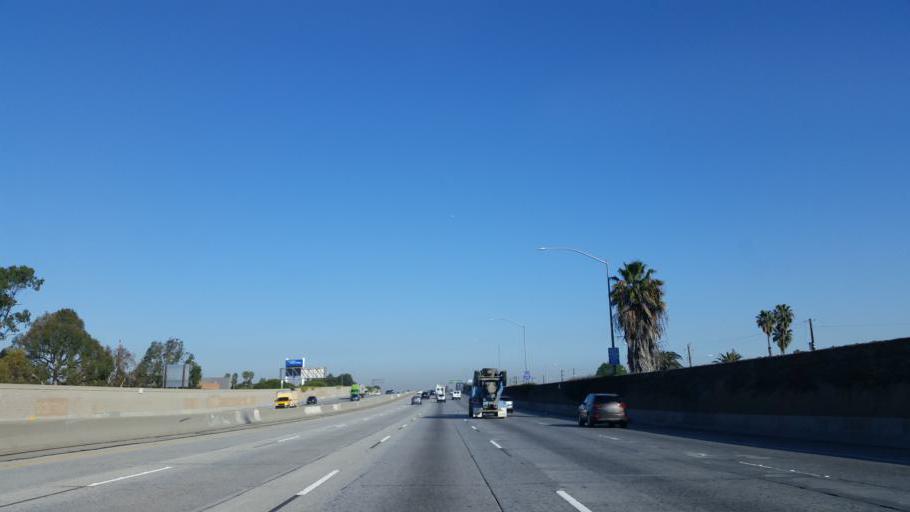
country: US
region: California
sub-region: Los Angeles County
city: Lomita
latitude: 33.7826
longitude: -118.2805
